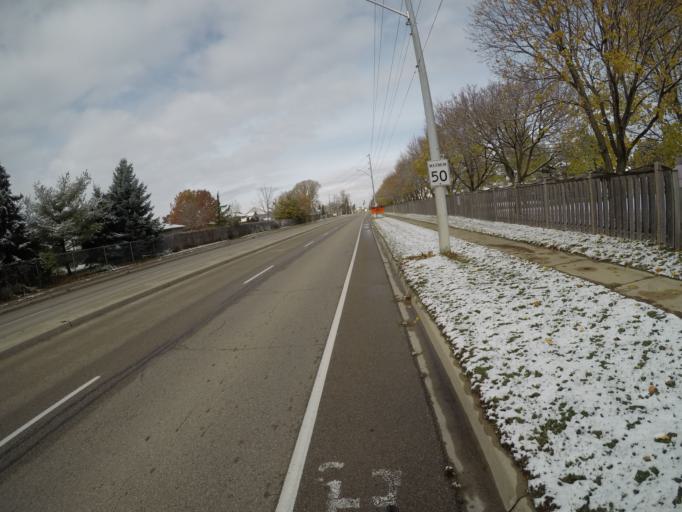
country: CA
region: Ontario
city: Waterloo
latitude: 43.4988
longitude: -80.4925
